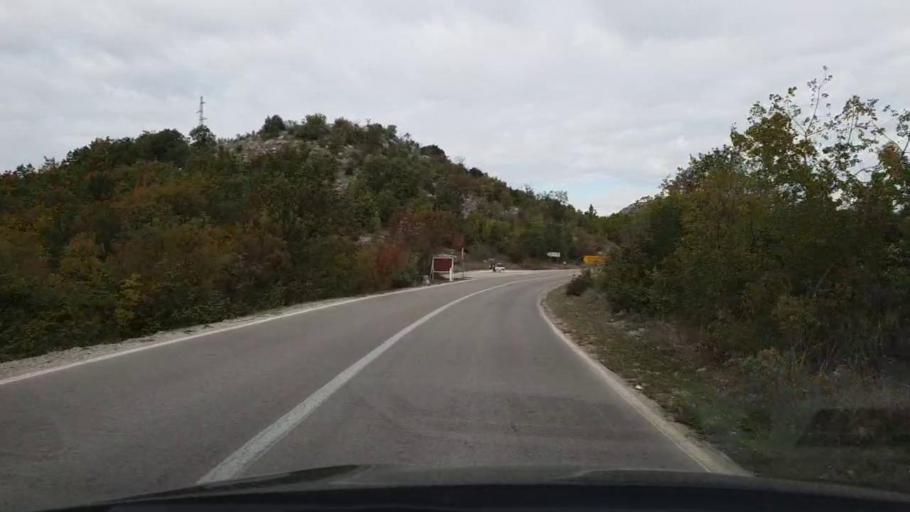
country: HR
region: Dubrovacko-Neretvanska
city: Cibaca
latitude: 42.6617
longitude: 18.2106
